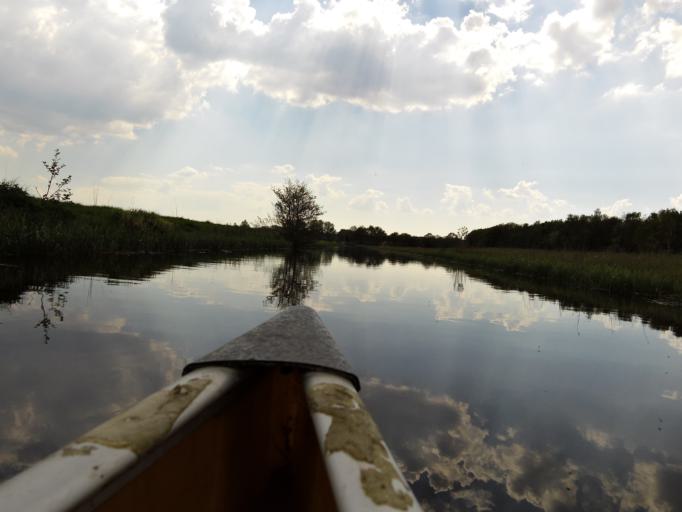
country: NL
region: South Holland
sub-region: Gemeente Wassenaar
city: Wassenaar
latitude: 52.1363
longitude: 4.4247
